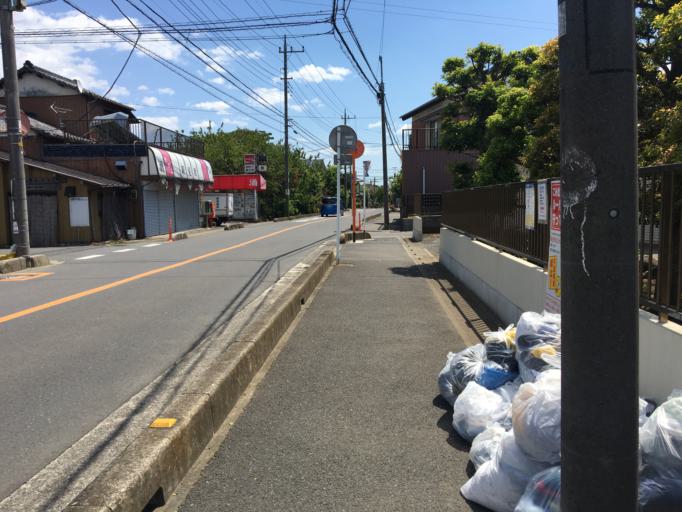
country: JP
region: Saitama
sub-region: Kawaguchi-shi
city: Hatogaya-honcho
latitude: 35.8461
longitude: 139.7534
